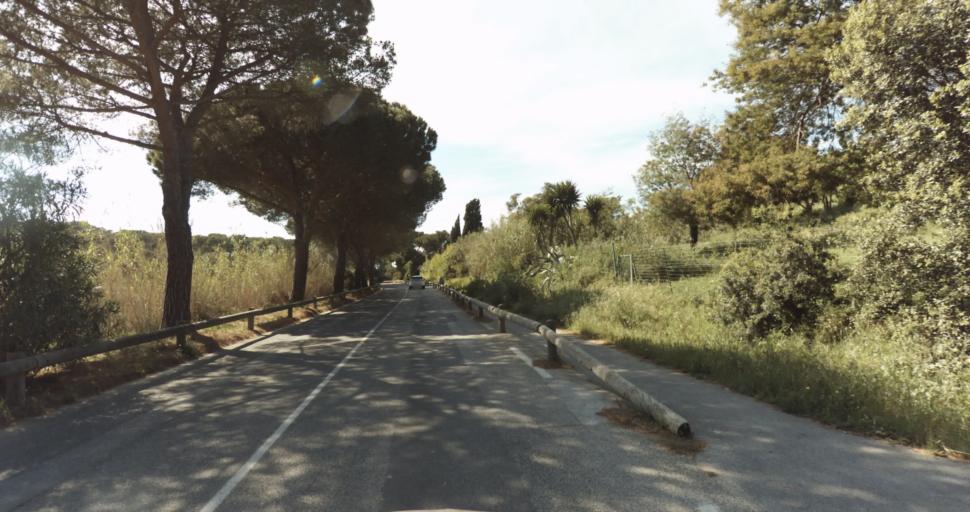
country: FR
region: Provence-Alpes-Cote d'Azur
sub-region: Departement du Var
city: Hyeres
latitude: 43.0326
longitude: 6.1495
